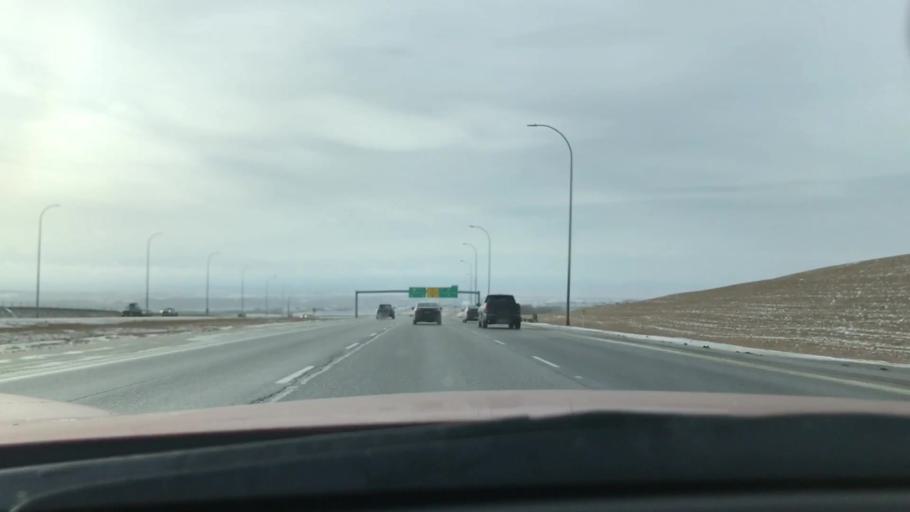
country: CA
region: Alberta
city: Calgary
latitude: 51.1381
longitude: -114.2148
